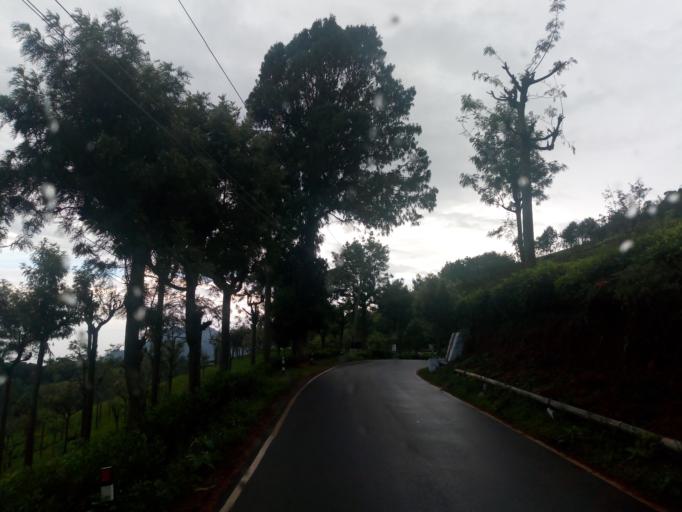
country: IN
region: Tamil Nadu
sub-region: Nilgiri
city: Wellington
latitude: 11.3574
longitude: 76.8327
